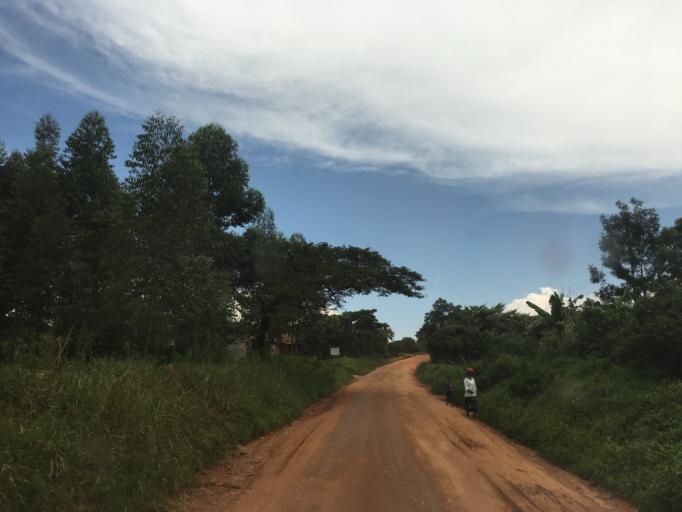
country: UG
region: Western Region
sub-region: Kibale District
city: Muhororo
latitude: 0.8288
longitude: 30.7416
